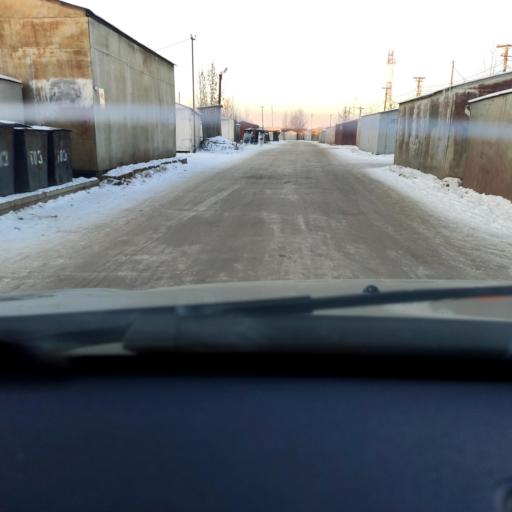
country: RU
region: Bashkortostan
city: Mikhaylovka
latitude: 54.7155
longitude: 55.8287
